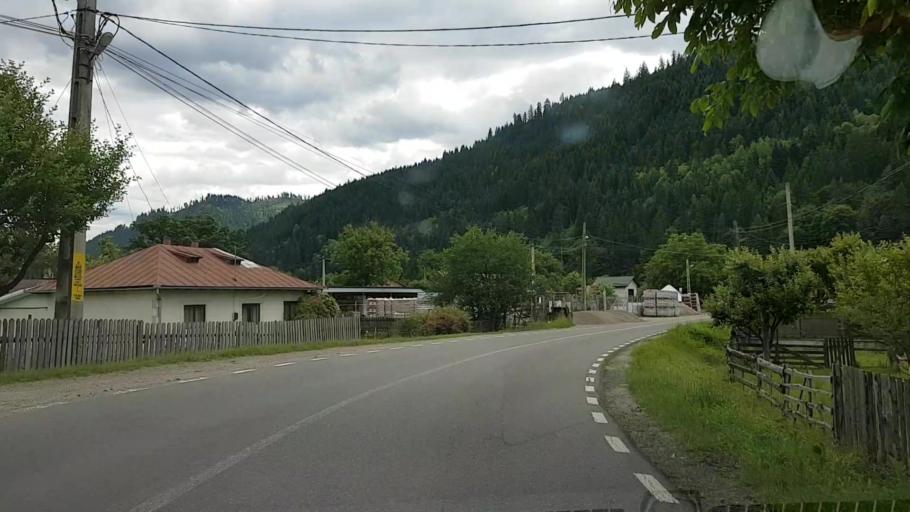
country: RO
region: Neamt
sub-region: Comuna Poiana Teiului
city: Poiana Teiului
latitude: 47.1112
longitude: 25.9319
